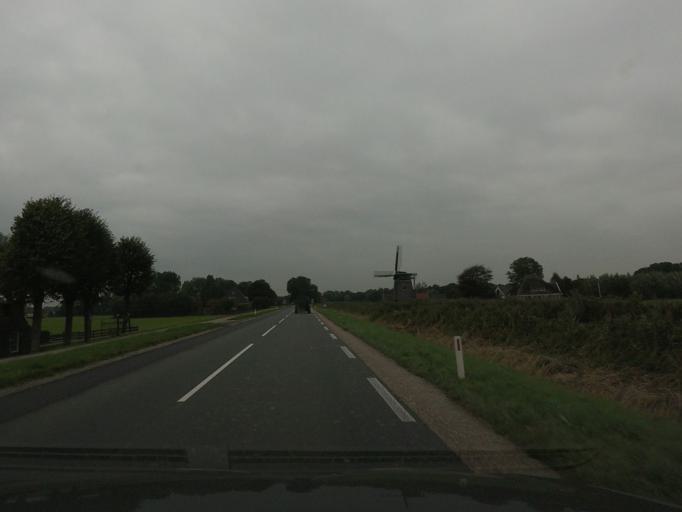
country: NL
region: North Holland
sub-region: Gemeente Heerhugowaard
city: Heerhugowaard
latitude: 52.7177
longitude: 4.8680
